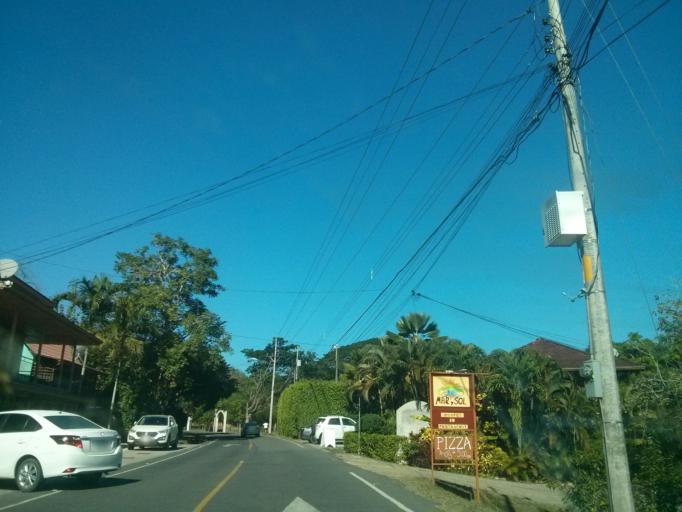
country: CR
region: Puntarenas
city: Paquera
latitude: 9.7197
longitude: -85.0206
